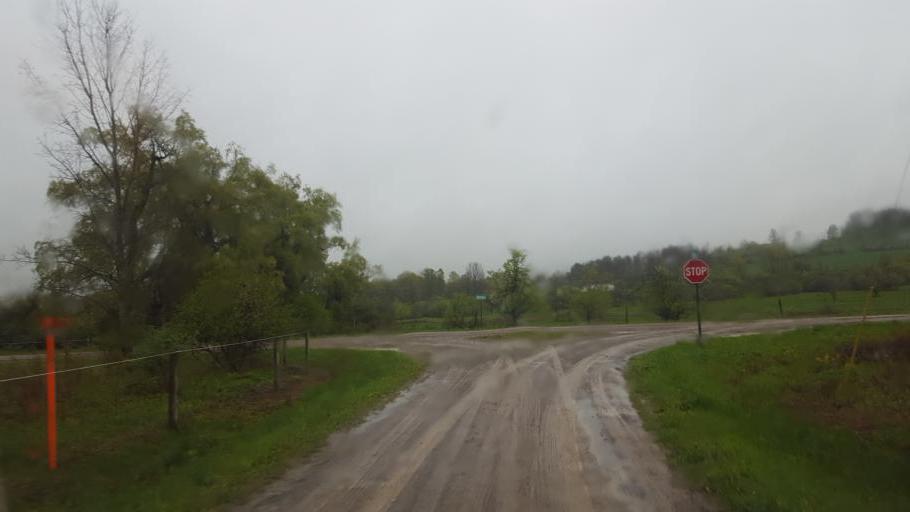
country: US
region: Pennsylvania
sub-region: Tioga County
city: Westfield
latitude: 42.0589
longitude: -77.4818
